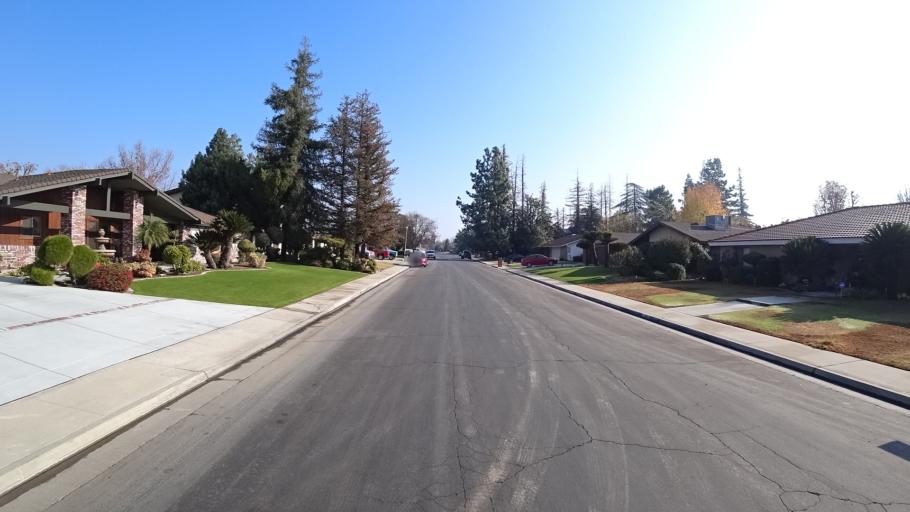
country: US
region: California
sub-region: Kern County
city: Greenacres
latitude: 35.3414
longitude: -119.0835
